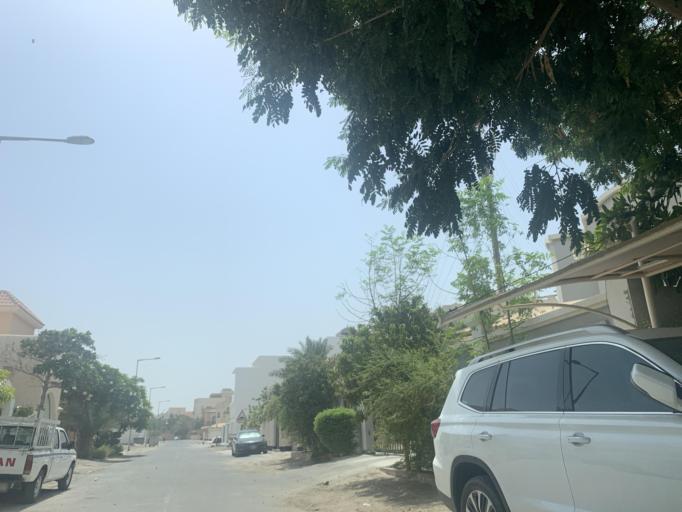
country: BH
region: Northern
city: Madinat `Isa
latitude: 26.1920
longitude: 50.4954
